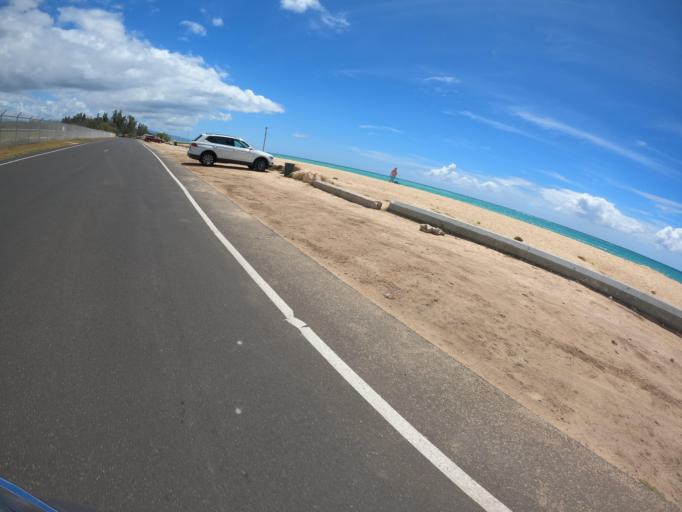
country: US
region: Hawaii
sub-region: Honolulu County
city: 'Ewa Villages
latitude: 21.3001
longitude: -158.0623
